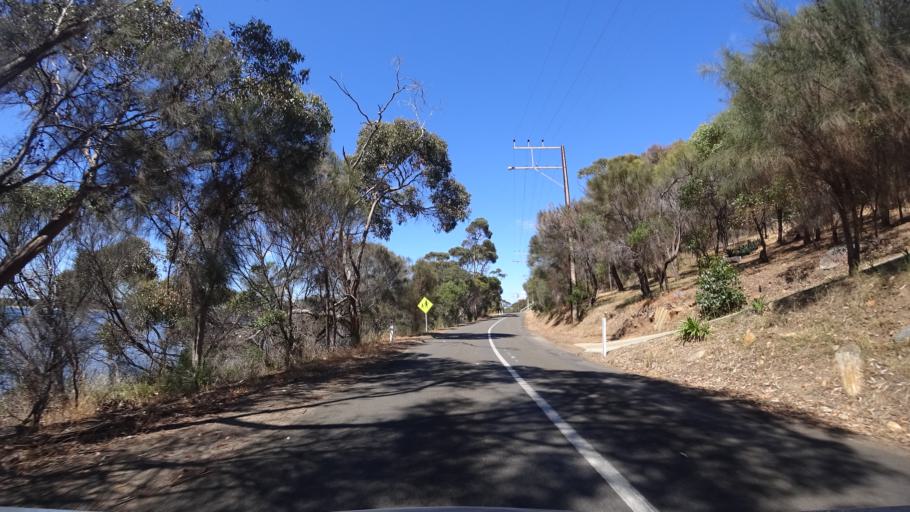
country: AU
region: South Australia
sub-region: Kangaroo Island
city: Kingscote
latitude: -35.7784
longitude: 137.7745
